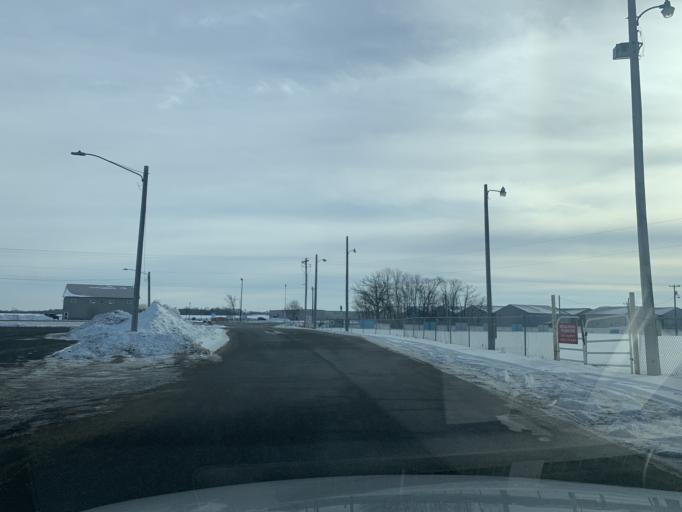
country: US
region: Minnesota
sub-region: Wright County
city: Buffalo
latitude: 45.1606
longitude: -93.8488
